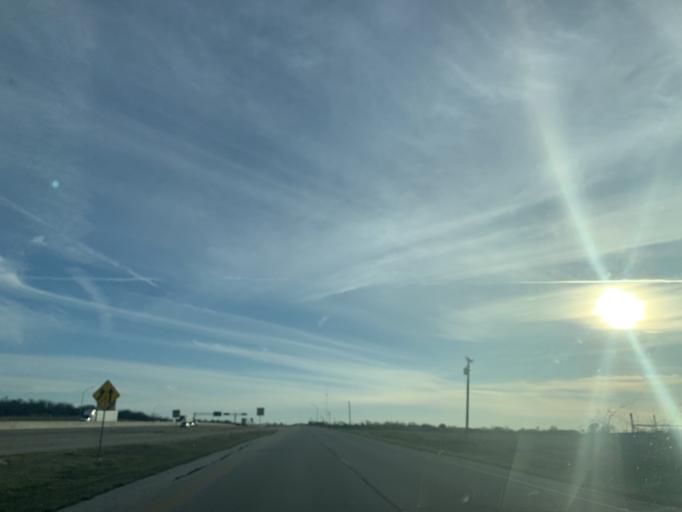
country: US
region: Texas
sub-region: Bell County
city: Salado
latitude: 30.8723
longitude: -97.5827
